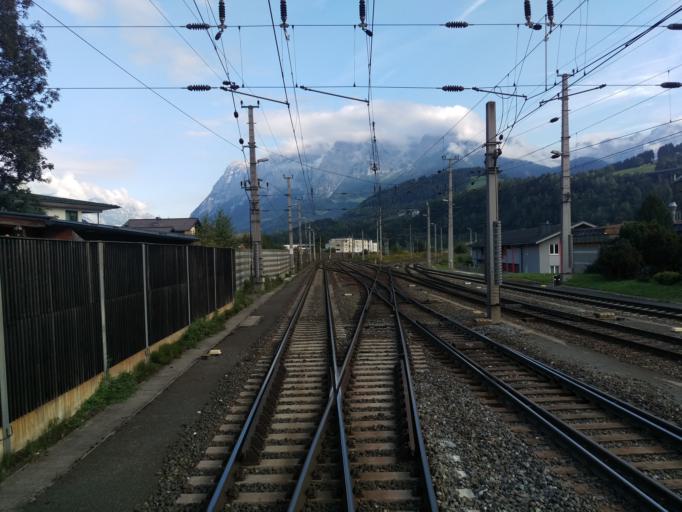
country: AT
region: Salzburg
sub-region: Politischer Bezirk Sankt Johann im Pongau
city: Bischofshofen
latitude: 47.4209
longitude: 13.2197
